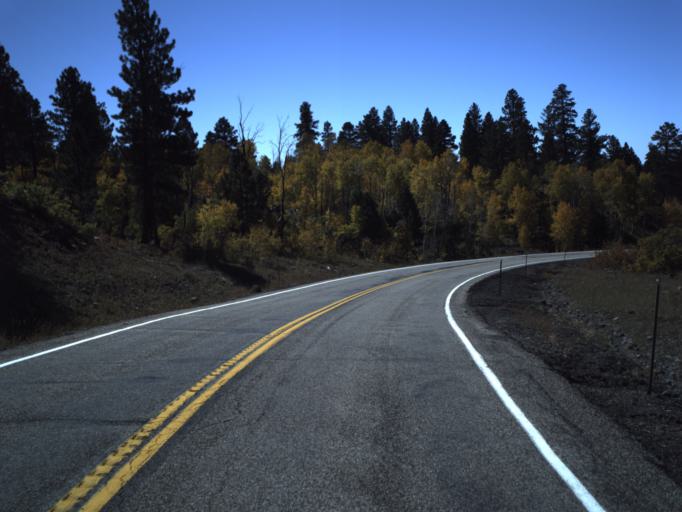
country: US
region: Utah
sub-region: Wayne County
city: Loa
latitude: 38.0049
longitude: -111.4052
